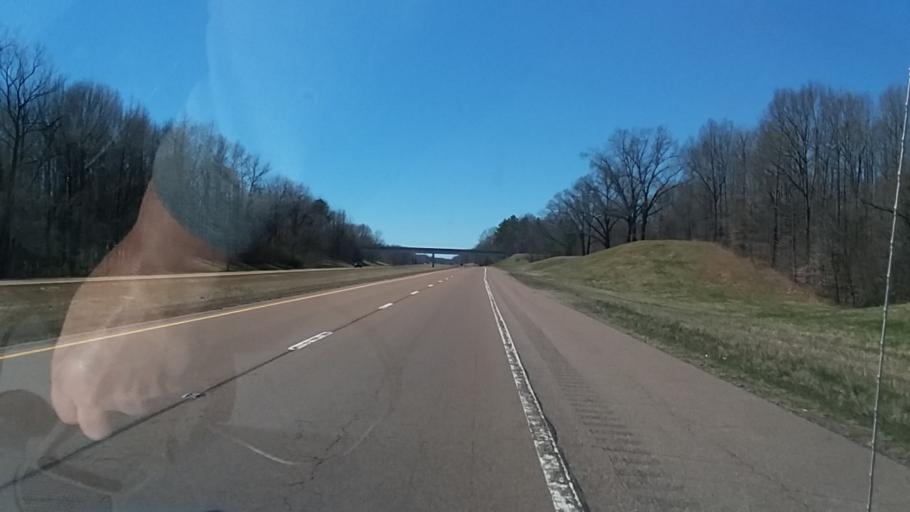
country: US
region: Tennessee
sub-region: Dyer County
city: Dyersburg
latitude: 36.0695
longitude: -89.4220
